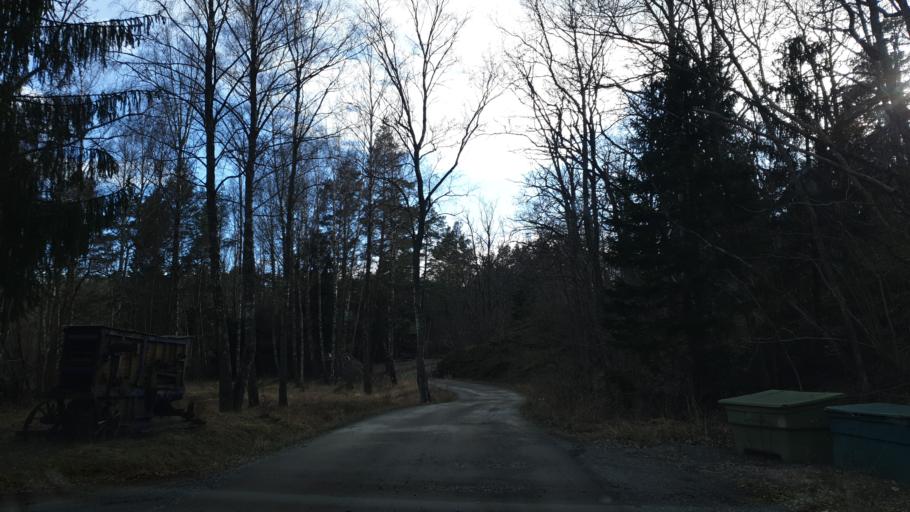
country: SE
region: Stockholm
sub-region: Varmdo Kommun
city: Holo
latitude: 59.3721
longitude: 18.6757
